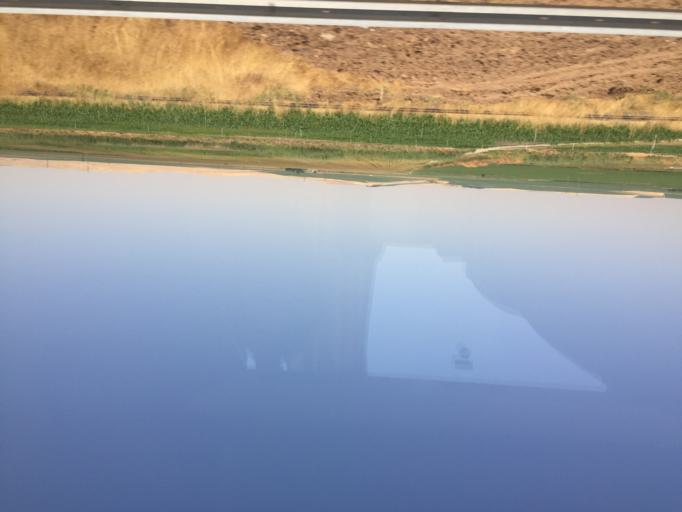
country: TR
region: Diyarbakir
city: Tepe
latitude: 37.8502
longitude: 40.7785
